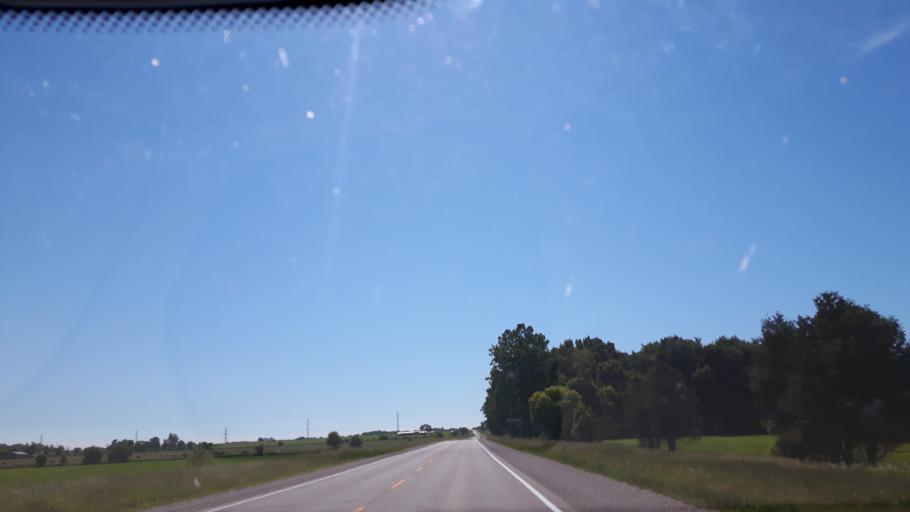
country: CA
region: Ontario
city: Bluewater
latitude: 43.4254
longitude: -81.5847
